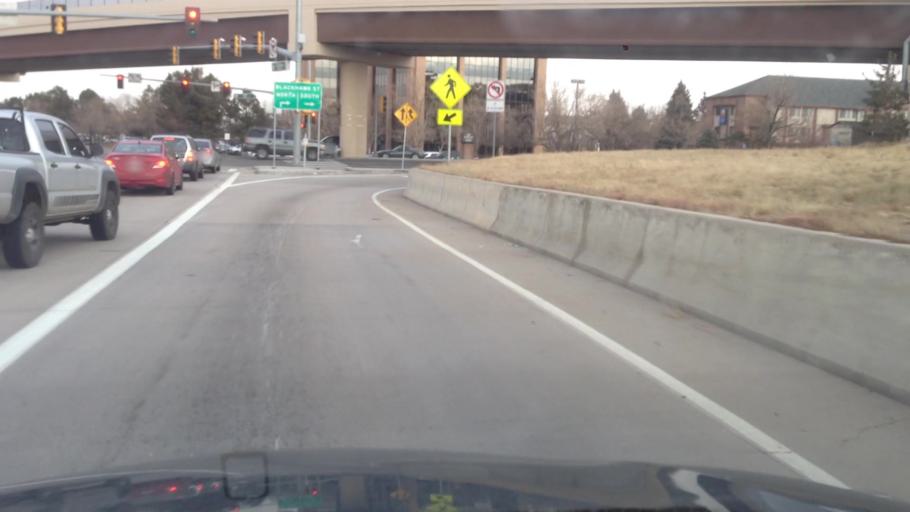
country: US
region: Colorado
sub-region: Adams County
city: Aurora
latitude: 39.6743
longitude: -104.8267
